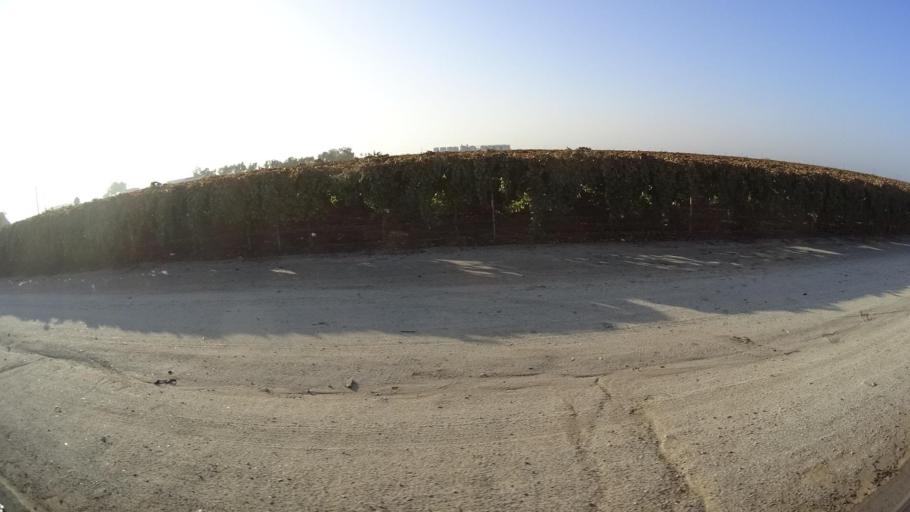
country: US
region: California
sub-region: Kern County
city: Delano
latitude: 35.7905
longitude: -119.1903
